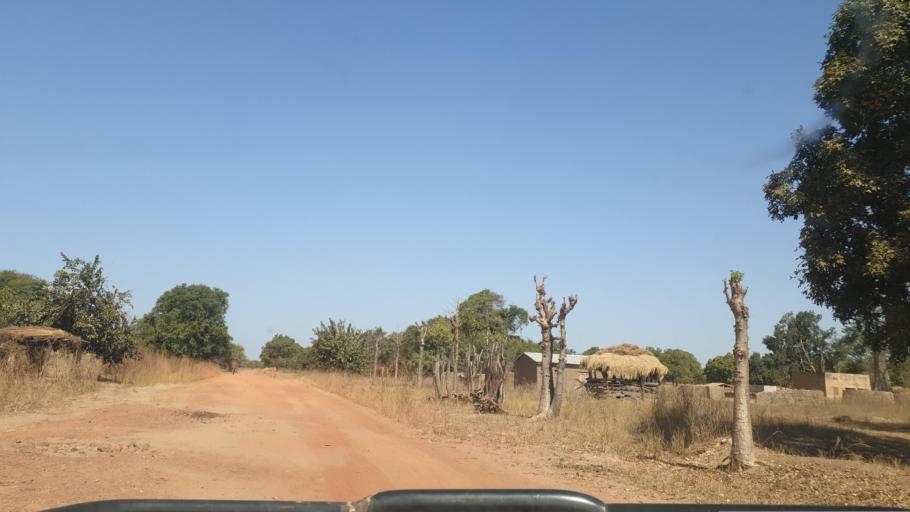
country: ML
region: Koulikoro
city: Dioila
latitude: 11.8963
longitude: -6.9804
